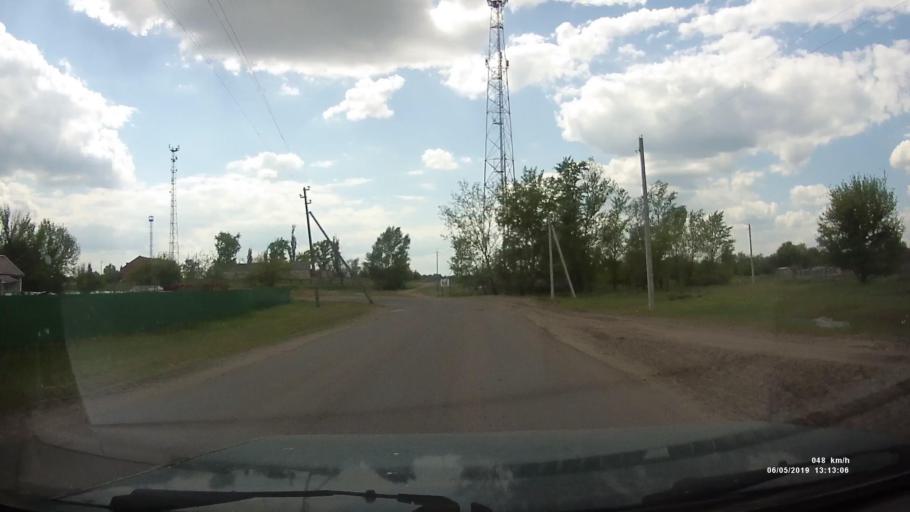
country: RU
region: Rostov
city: Ust'-Donetskiy
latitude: 47.7548
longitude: 40.9395
